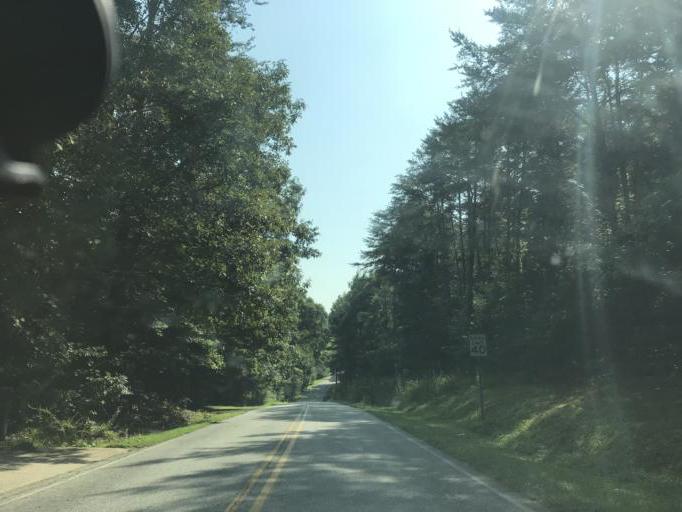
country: US
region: Georgia
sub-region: Forsyth County
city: Cumming
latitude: 34.2304
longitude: -84.1189
